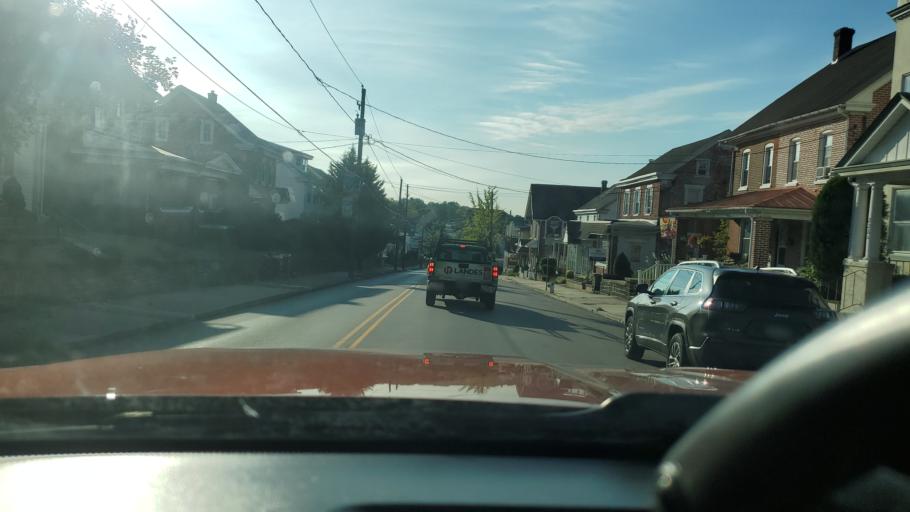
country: US
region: Pennsylvania
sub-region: Montgomery County
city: Souderton
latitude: 40.3125
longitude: -75.3262
